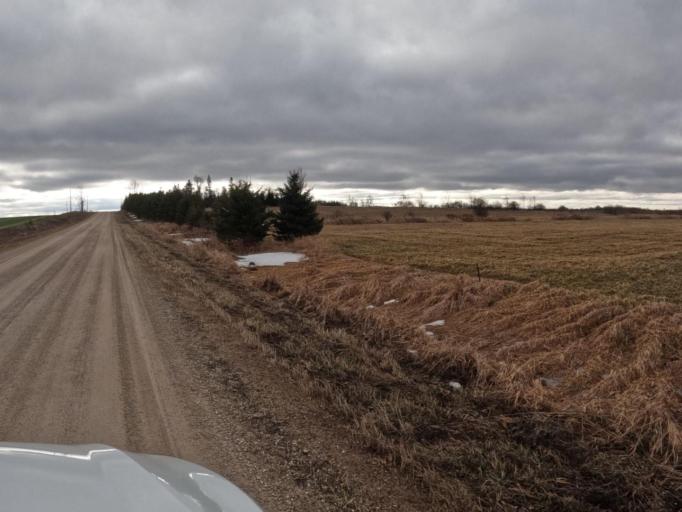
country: CA
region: Ontario
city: Shelburne
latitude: 43.9784
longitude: -80.4046
